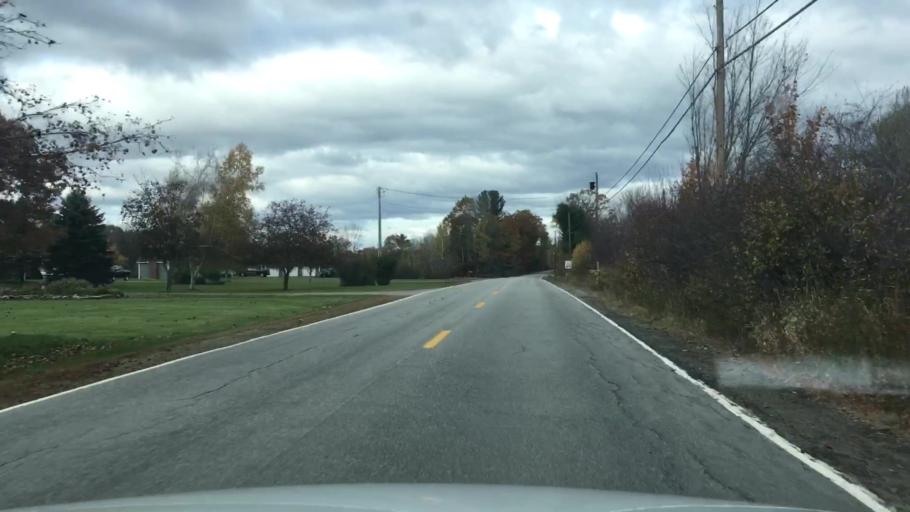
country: US
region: Maine
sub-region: Androscoggin County
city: Sabattus
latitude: 44.1559
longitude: -70.0801
